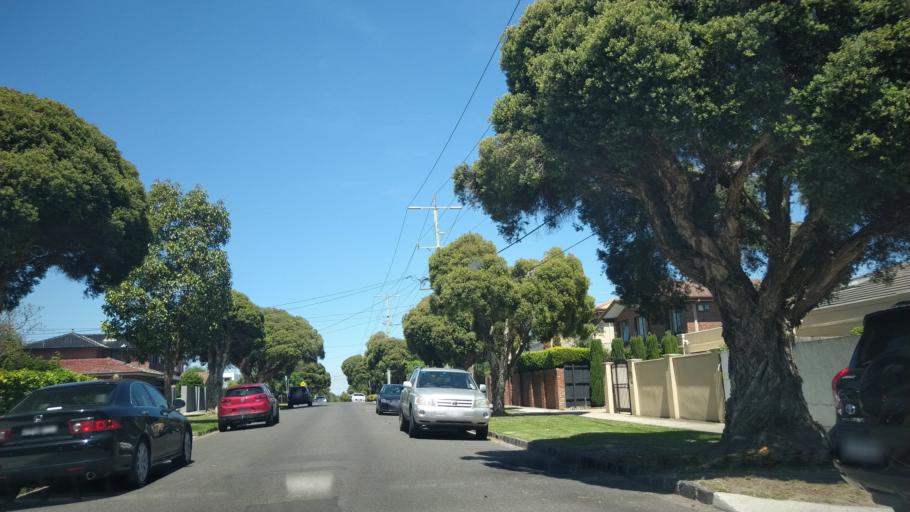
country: AU
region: Victoria
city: Ormond
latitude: -37.8945
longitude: 145.0320
